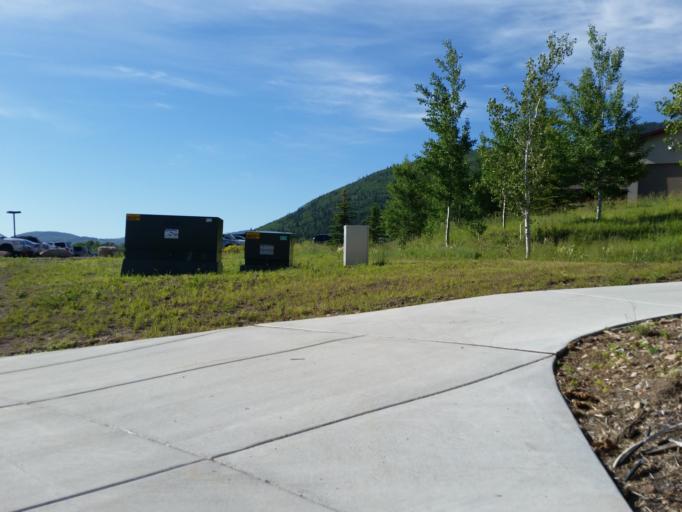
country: US
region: Utah
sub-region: Summit County
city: Snyderville
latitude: 40.6873
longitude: -111.5487
